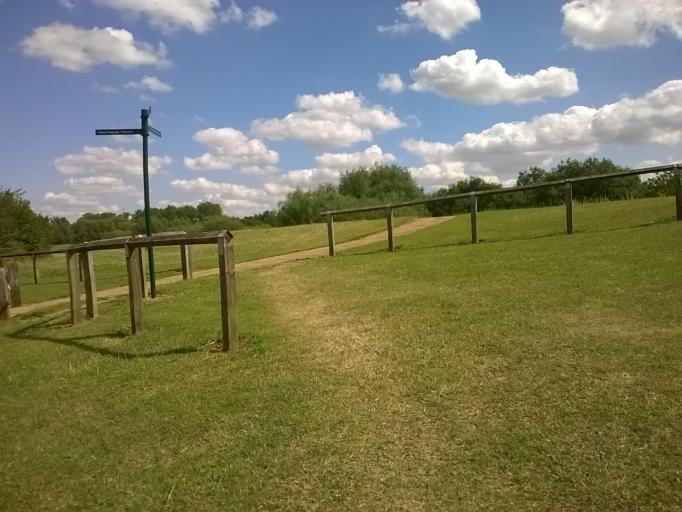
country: GB
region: England
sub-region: Milton Keynes
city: Broughton
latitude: 52.0550
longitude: -0.7152
